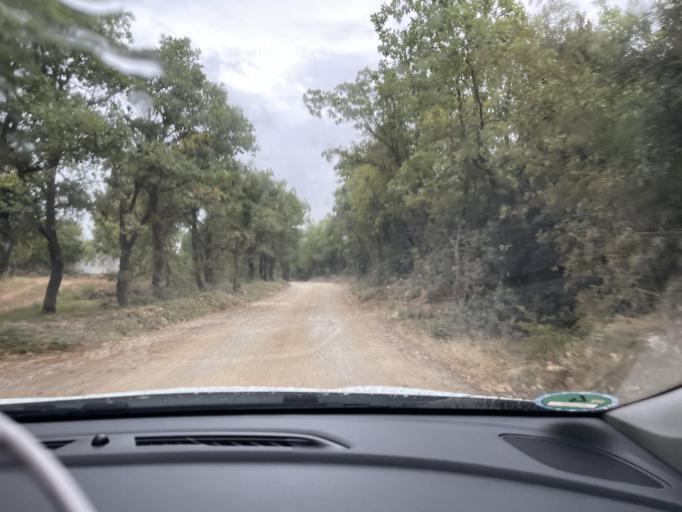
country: HR
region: Istarska
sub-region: Grad Rovinj
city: Rovinj
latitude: 45.0453
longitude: 13.7126
